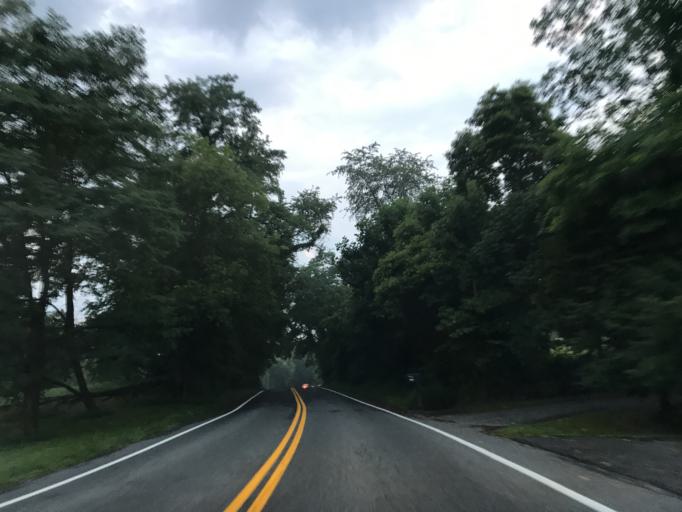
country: US
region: Maryland
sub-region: Harford County
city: Fallston
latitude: 39.5215
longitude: -76.3999
